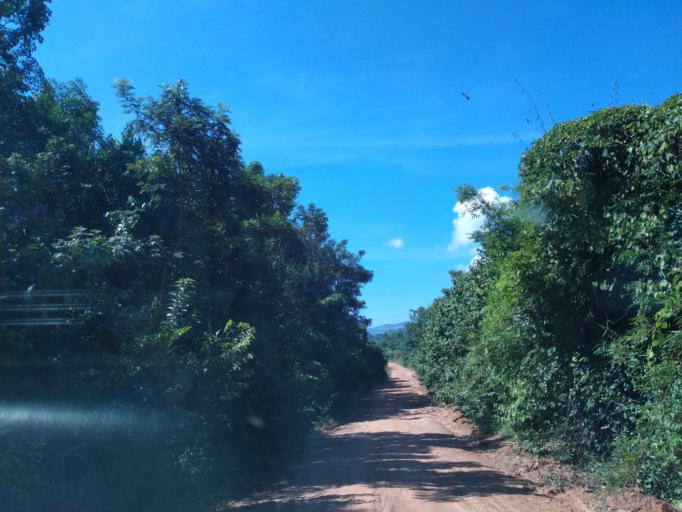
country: LA
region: Vientiane
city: Muang Phon-Hong
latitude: 18.6206
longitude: 102.8695
